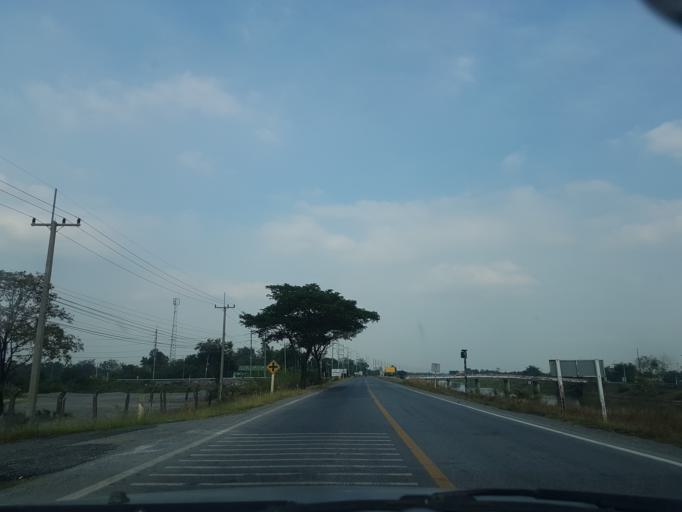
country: TH
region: Phra Nakhon Si Ayutthaya
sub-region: Amphoe Tha Ruea
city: Tha Ruea
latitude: 14.5292
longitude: 100.7433
